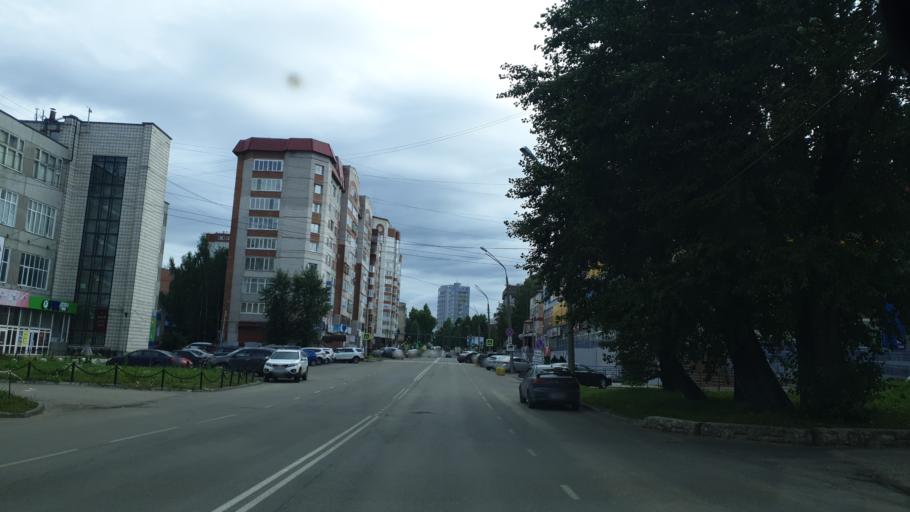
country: RU
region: Komi Republic
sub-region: Syktyvdinskiy Rayon
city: Syktyvkar
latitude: 61.6742
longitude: 50.8245
